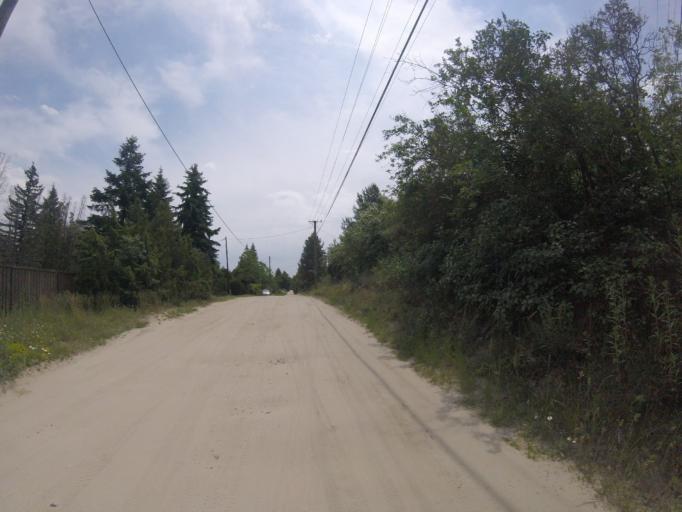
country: HU
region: Pest
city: Leanyfalu
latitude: 47.7178
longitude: 19.1108
